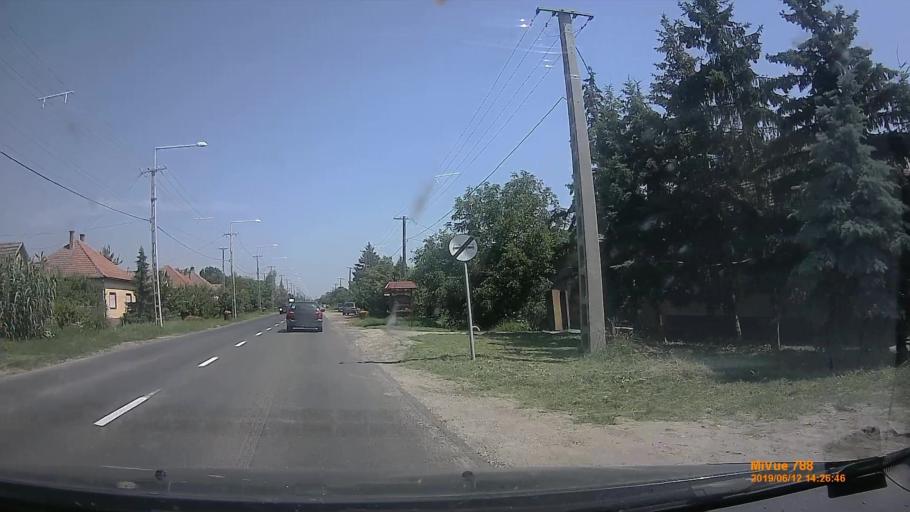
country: HU
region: Csongrad
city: Maroslele
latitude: 46.2196
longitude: 20.3479
